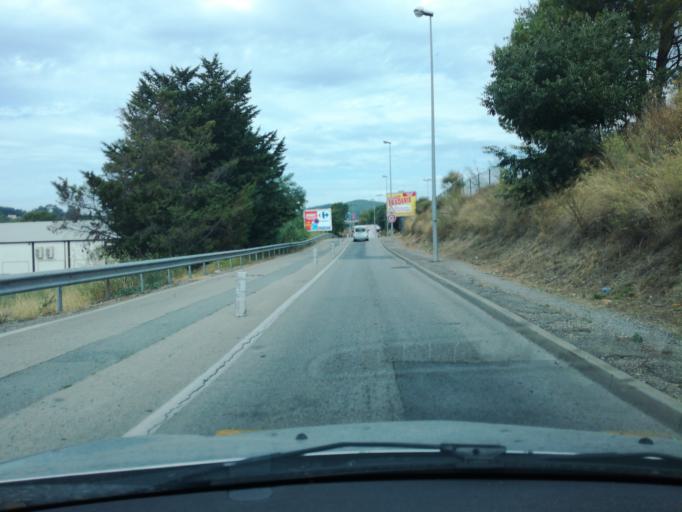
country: FR
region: Provence-Alpes-Cote d'Azur
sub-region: Departement du Var
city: Draguignan
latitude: 43.5267
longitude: 6.4543
